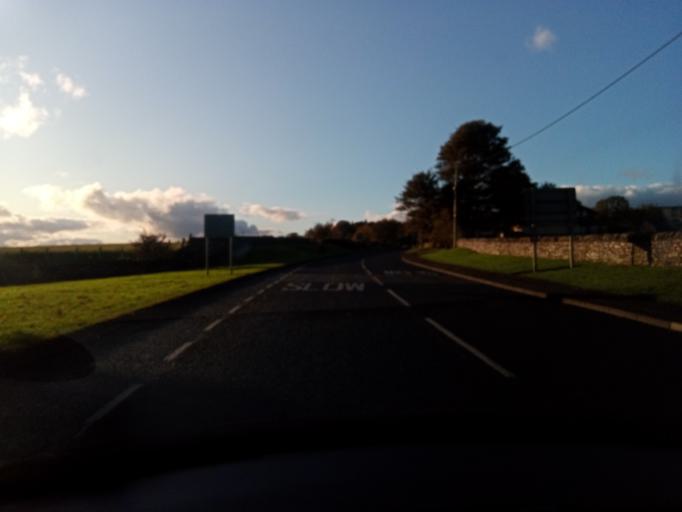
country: GB
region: England
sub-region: County Durham
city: Stanhope
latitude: 54.7487
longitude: -2.0196
